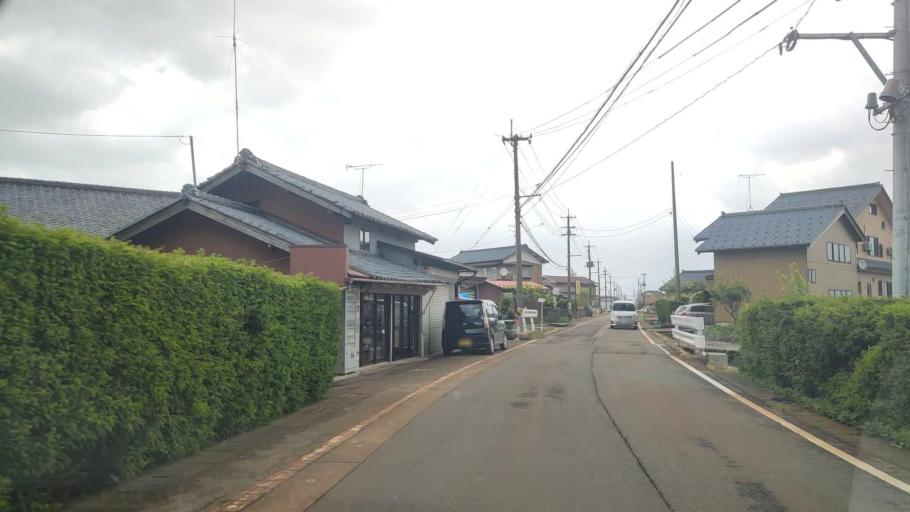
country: JP
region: Niigata
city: Gosen
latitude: 37.7329
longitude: 139.1624
